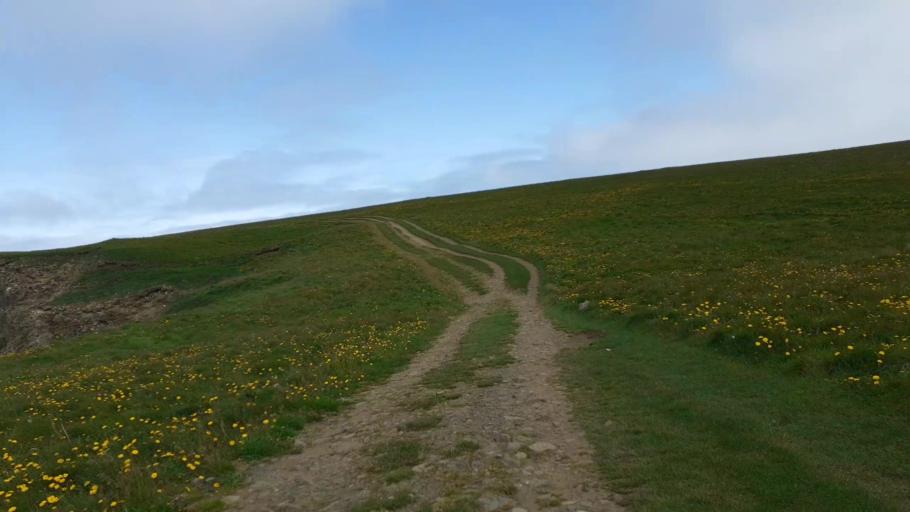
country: IS
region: Northeast
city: Dalvik
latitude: 66.5531
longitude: -18.0145
